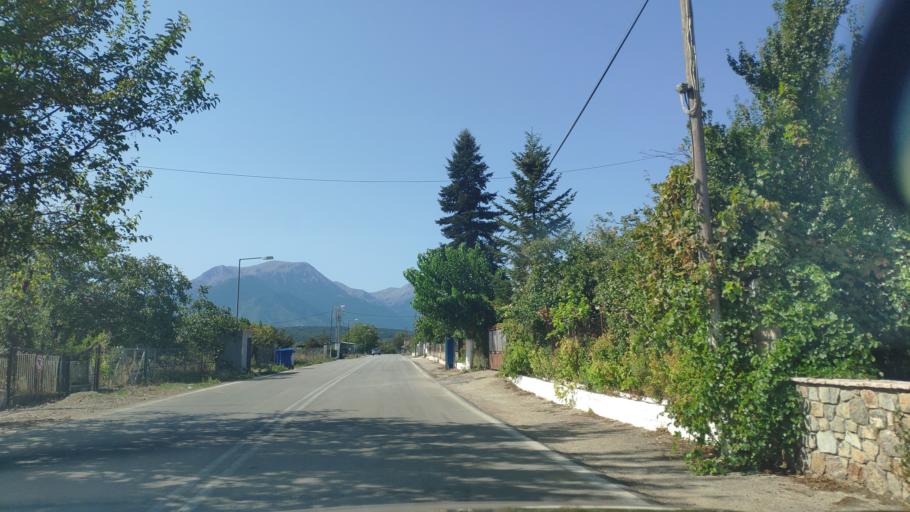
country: GR
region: Peloponnese
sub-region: Nomos Korinthias
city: Nemea
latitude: 37.8726
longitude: 22.4700
